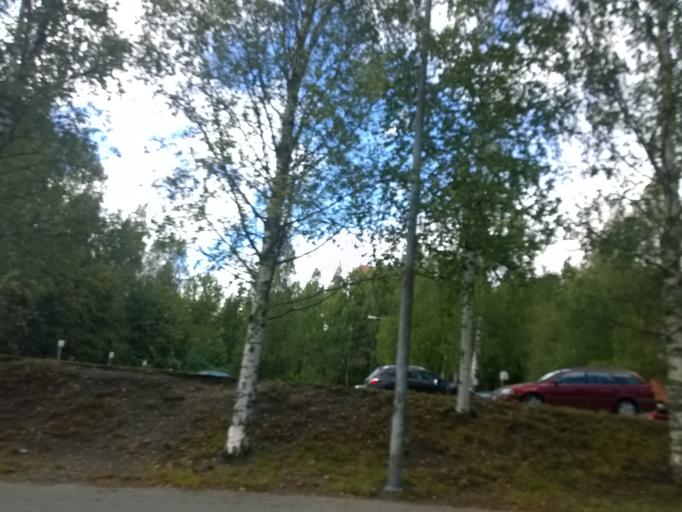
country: FI
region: Pirkanmaa
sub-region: Tampere
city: Tampere
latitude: 61.4448
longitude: 23.8386
